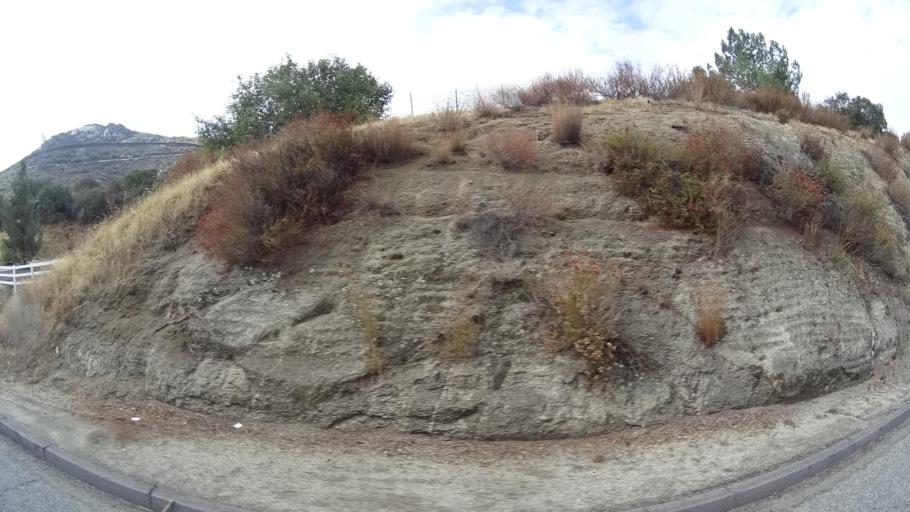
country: MX
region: Baja California
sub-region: Tecate
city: Hacienda Tecate
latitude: 32.5901
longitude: -116.5217
